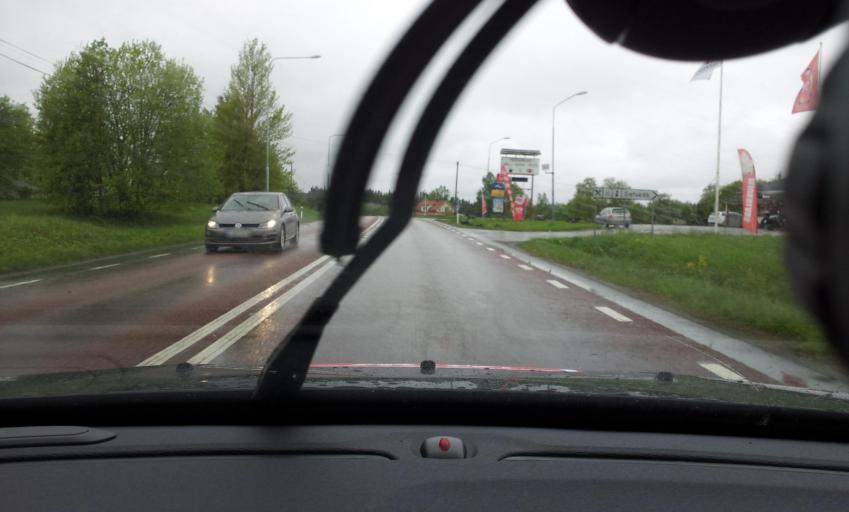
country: SE
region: Jaemtland
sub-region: Bergs Kommun
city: Hoverberg
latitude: 62.9116
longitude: 14.5246
